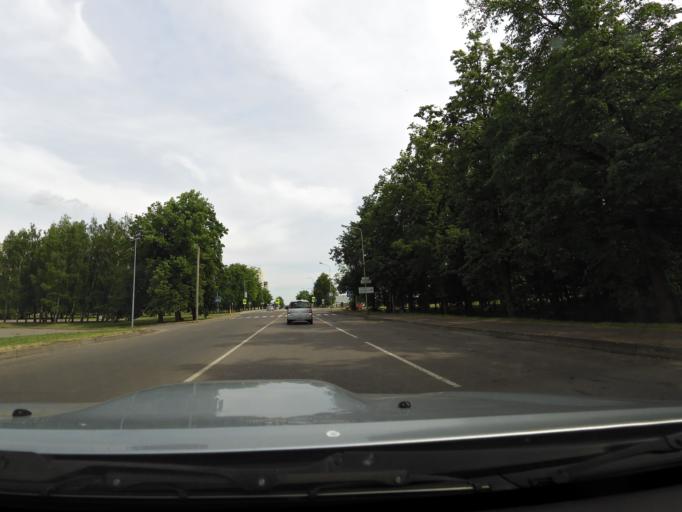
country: LT
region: Marijampoles apskritis
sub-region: Marijampole Municipality
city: Marijampole
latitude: 54.5641
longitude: 23.3284
